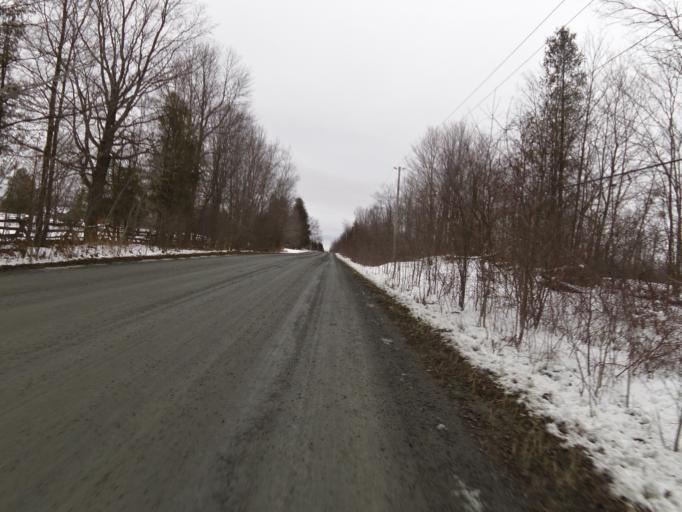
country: CA
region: Ontario
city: Carleton Place
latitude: 45.1099
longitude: -76.2513
